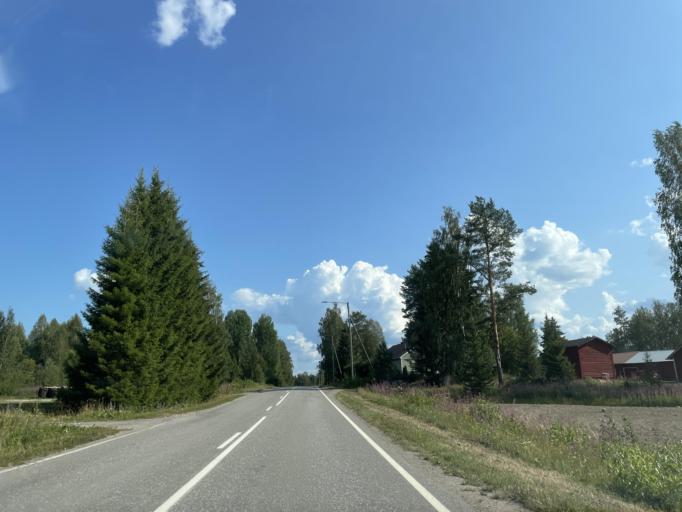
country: FI
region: Central Finland
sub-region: Saarijaervi-Viitasaari
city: Pihtipudas
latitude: 63.3612
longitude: 25.7460
